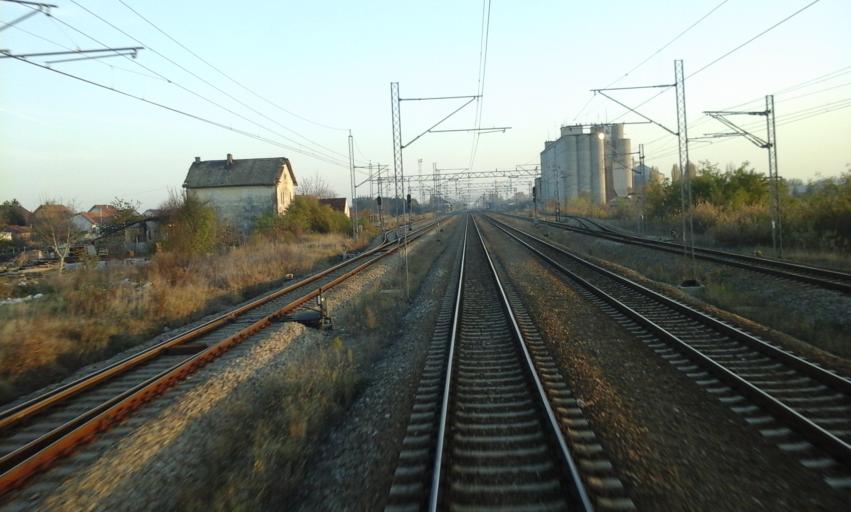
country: RS
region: Autonomna Pokrajina Vojvodina
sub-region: Sremski Okrug
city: Stara Pazova
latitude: 44.9914
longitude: 20.1339
